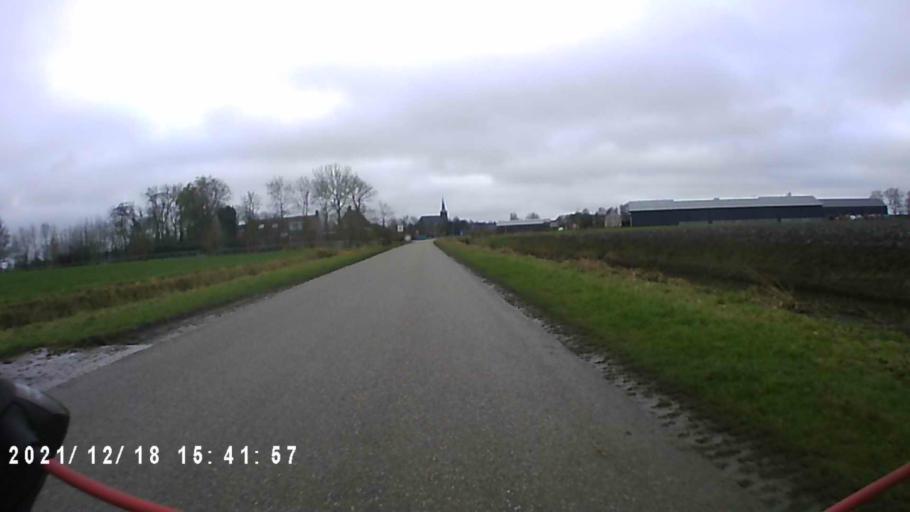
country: NL
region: Friesland
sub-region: Gemeente Dongeradeel
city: Anjum
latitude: 53.3343
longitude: 6.1055
